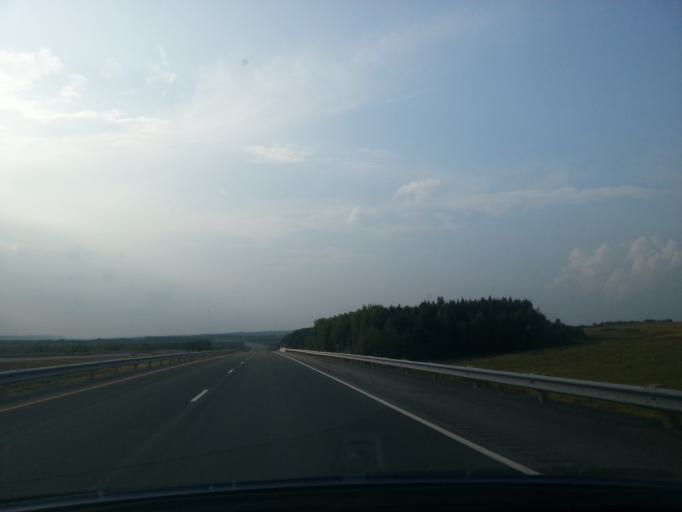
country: CA
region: New Brunswick
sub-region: Madawaska County
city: Saint-Leonard
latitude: 47.1263
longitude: -67.8550
